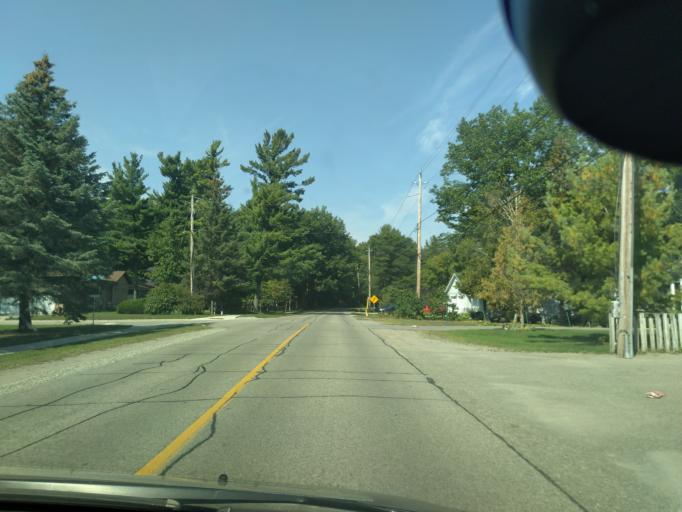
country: CA
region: Ontario
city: Newmarket
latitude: 44.1210
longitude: -79.5064
